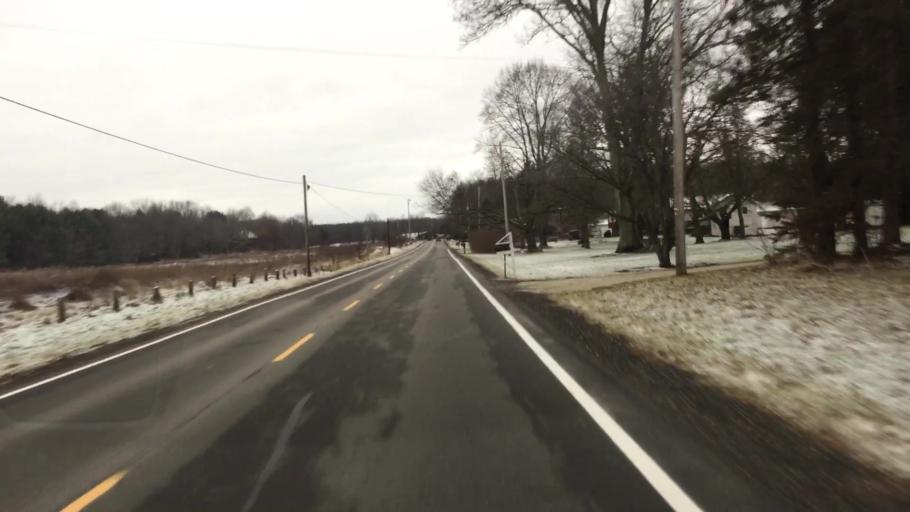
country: US
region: Ohio
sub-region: Summit County
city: Norton
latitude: 41.0724
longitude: -81.6329
